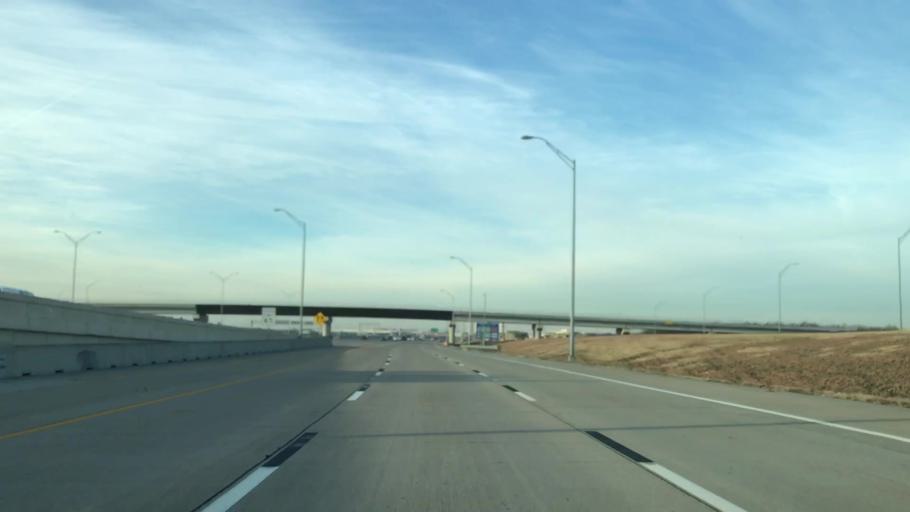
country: US
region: Texas
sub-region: Tarrant County
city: Grapevine
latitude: 32.9310
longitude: -97.0477
